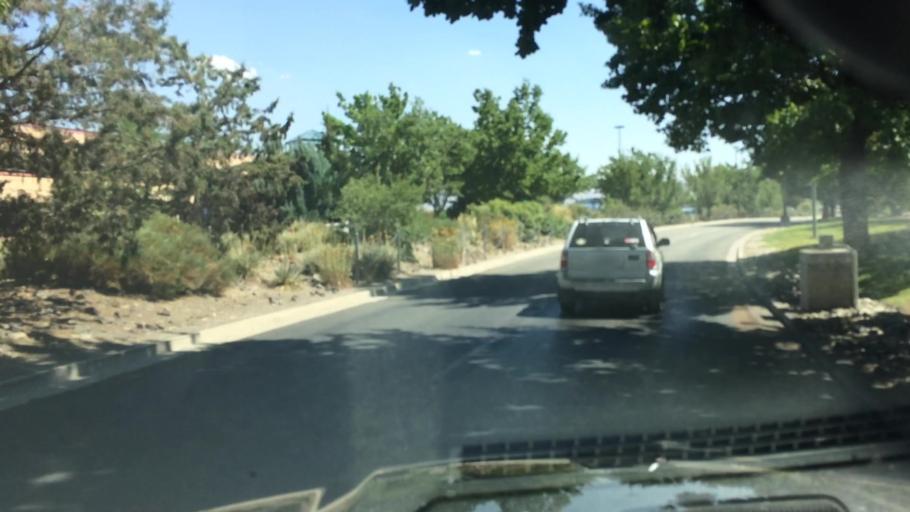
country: US
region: Nevada
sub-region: Washoe County
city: Sparks
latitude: 39.5056
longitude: -119.7776
